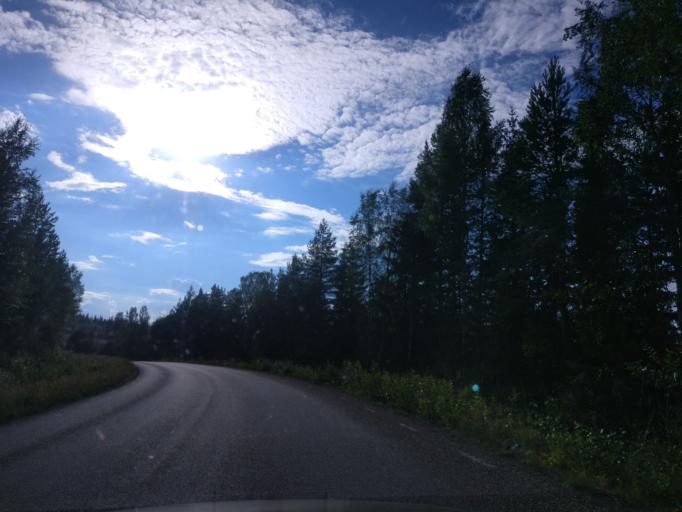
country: SE
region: Dalarna
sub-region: Ludvika Kommun
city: Ludvika
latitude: 60.2919
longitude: 15.1324
